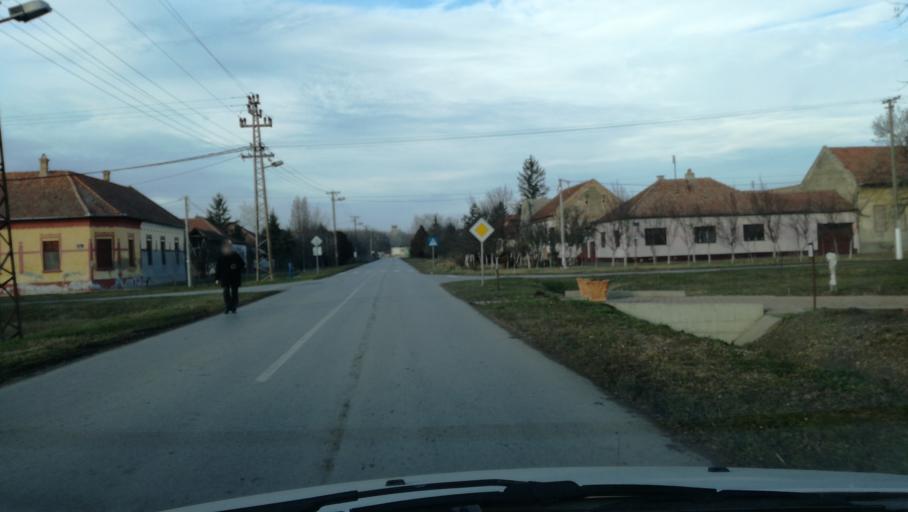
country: RS
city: Banatsko Veliko Selo
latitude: 45.8173
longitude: 20.6083
